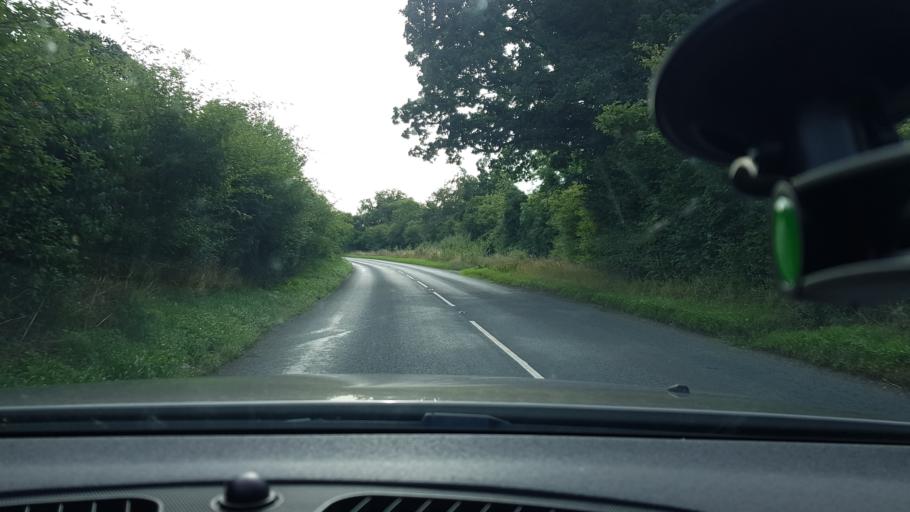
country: GB
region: England
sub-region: Wiltshire
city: Chilton Foliat
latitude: 51.4377
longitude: -1.5690
